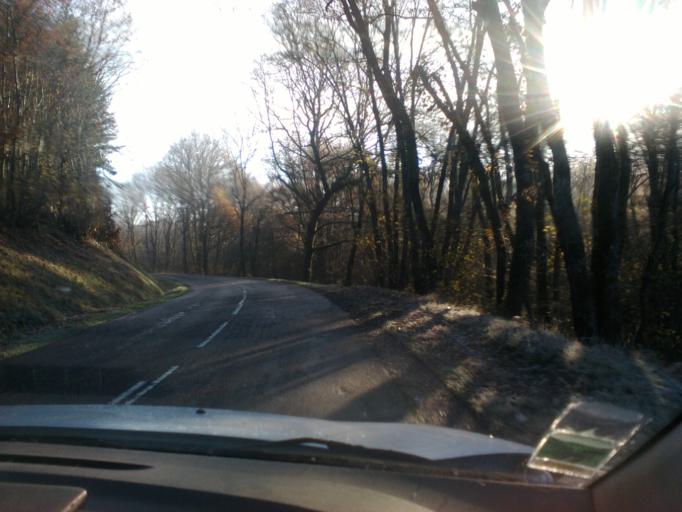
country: FR
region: Lorraine
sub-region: Departement des Vosges
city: Uzemain
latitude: 48.0577
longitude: 6.3507
